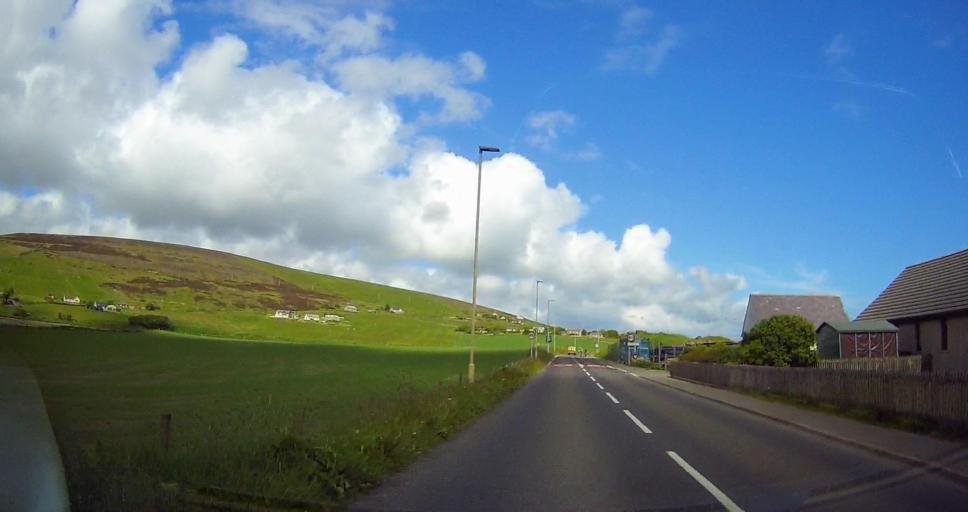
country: GB
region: Scotland
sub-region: Orkney Islands
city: Orkney
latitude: 59.0088
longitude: -3.1159
